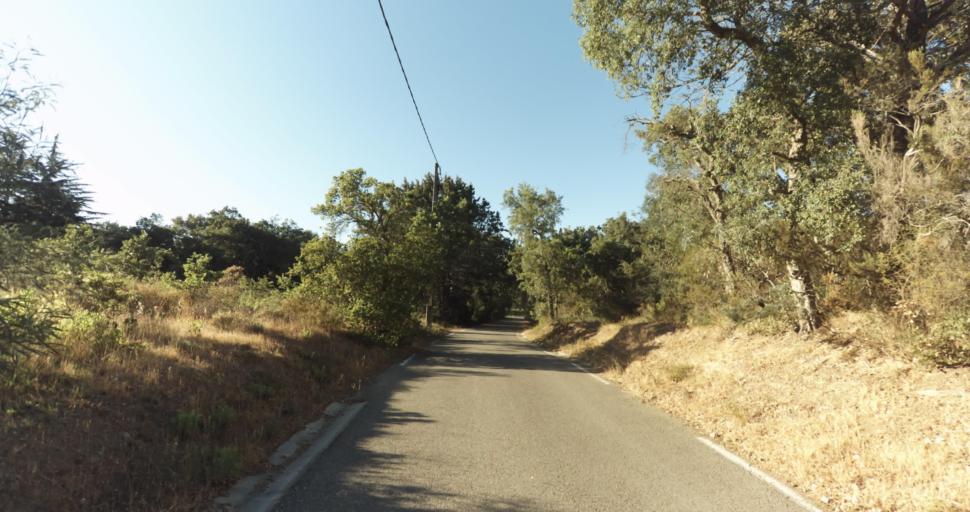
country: FR
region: Provence-Alpes-Cote d'Azur
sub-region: Departement du Var
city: Gassin
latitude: 43.2314
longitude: 6.5941
